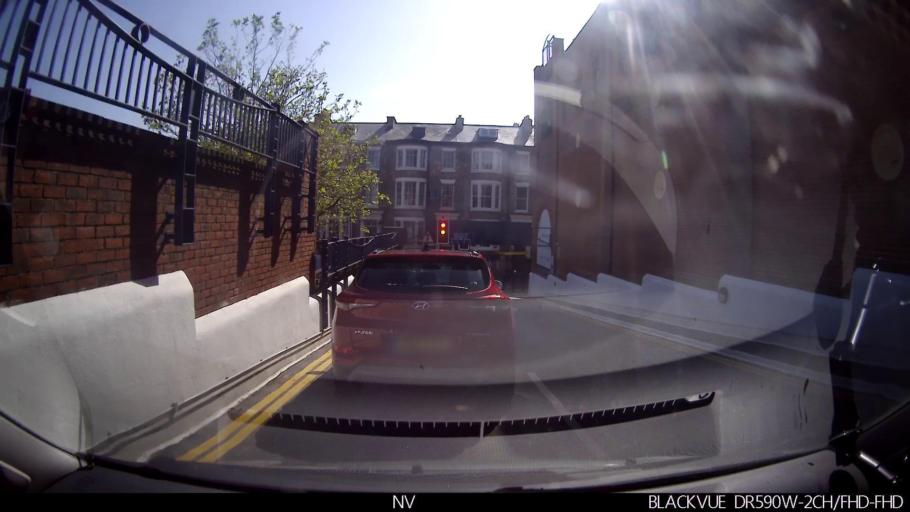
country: GB
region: England
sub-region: North Yorkshire
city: Scarborough
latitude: 54.2805
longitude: -0.4020
